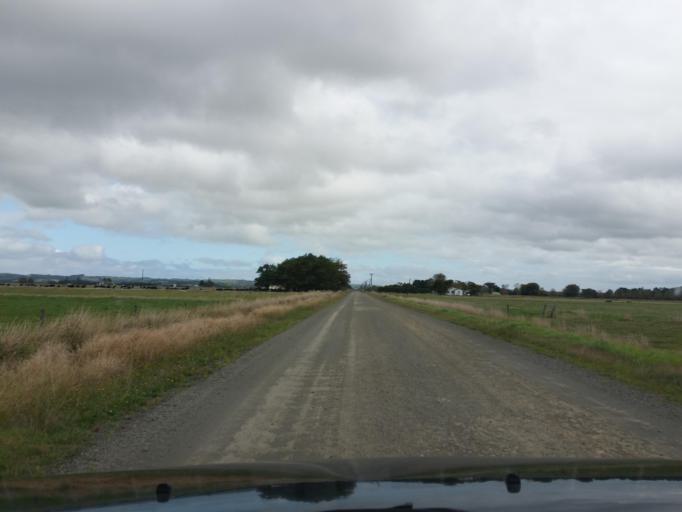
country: NZ
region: Northland
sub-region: Kaipara District
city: Dargaville
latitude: -36.0866
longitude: 174.0291
